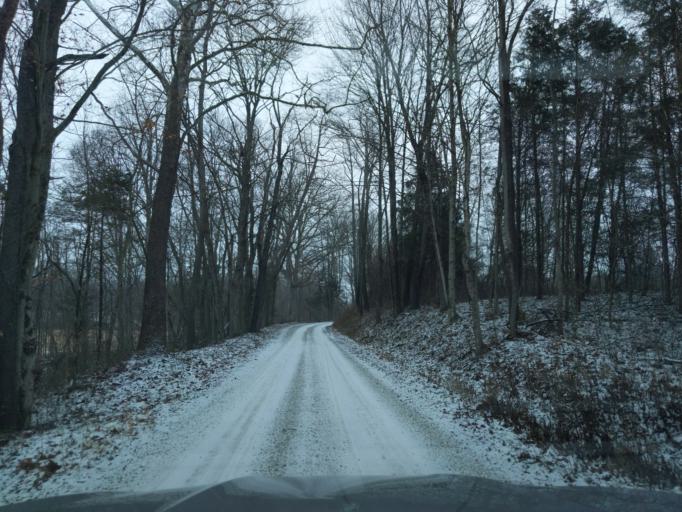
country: US
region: Indiana
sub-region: Decatur County
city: Westport
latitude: 39.2097
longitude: -85.4444
